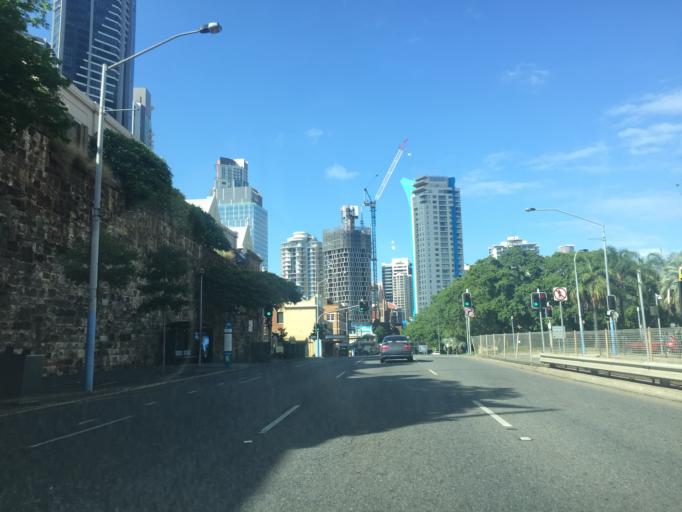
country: AU
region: Queensland
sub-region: Brisbane
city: Fortitude Valley
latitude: -27.4604
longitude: 153.0331
